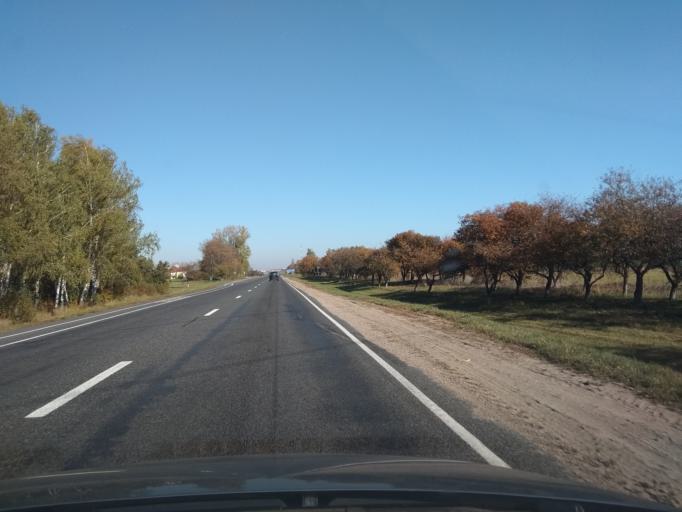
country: BY
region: Brest
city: Kobryn
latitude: 52.1707
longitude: 24.3188
